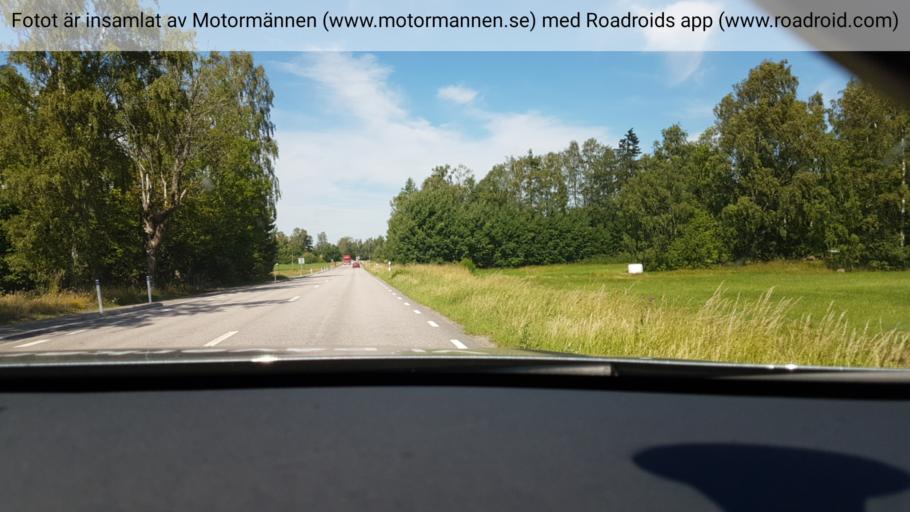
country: SE
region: Vaestra Goetaland
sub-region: Skovde Kommun
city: Stopen
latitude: 58.5032
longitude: 13.9703
